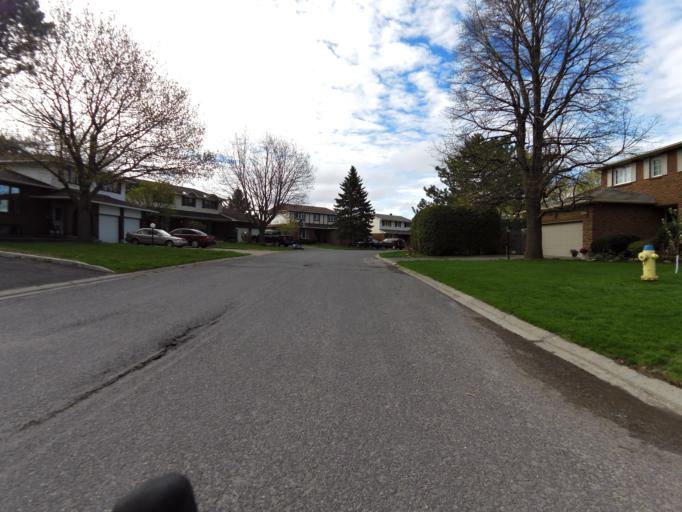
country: CA
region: Ontario
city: Bells Corners
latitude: 45.2919
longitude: -75.7439
